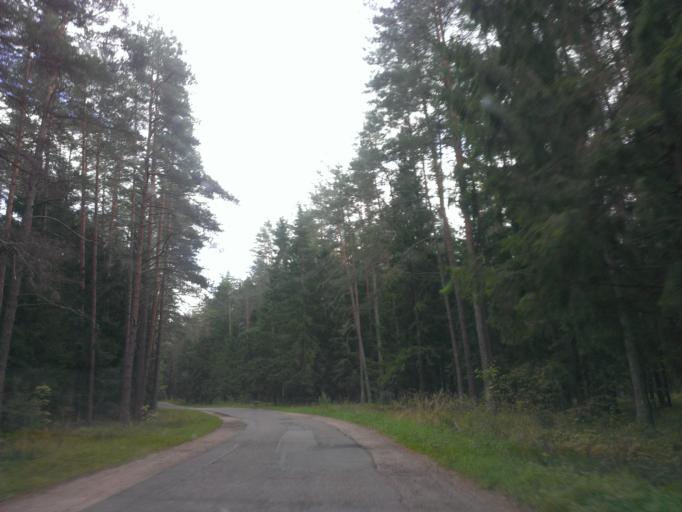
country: LV
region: Incukalns
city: Vangazi
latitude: 57.0969
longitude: 24.5354
